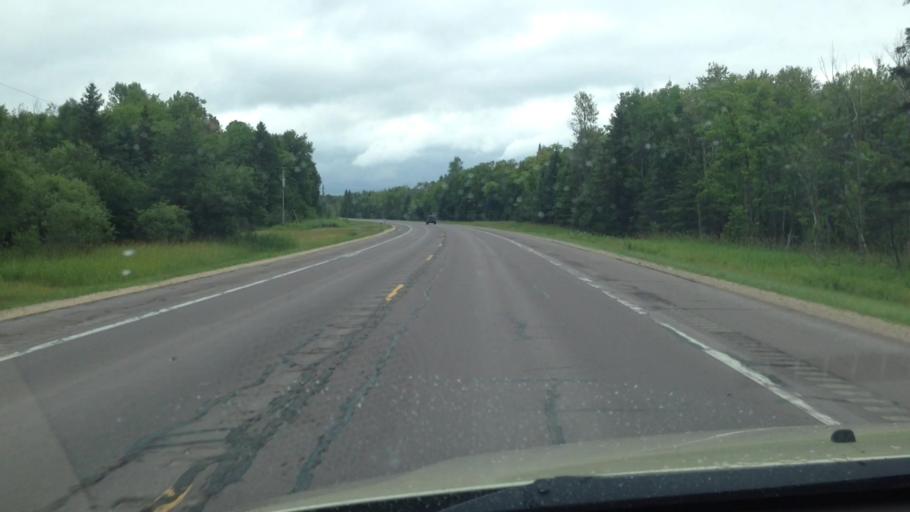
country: US
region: Michigan
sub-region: Schoolcraft County
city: Manistique
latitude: 46.0592
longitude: -85.9592
